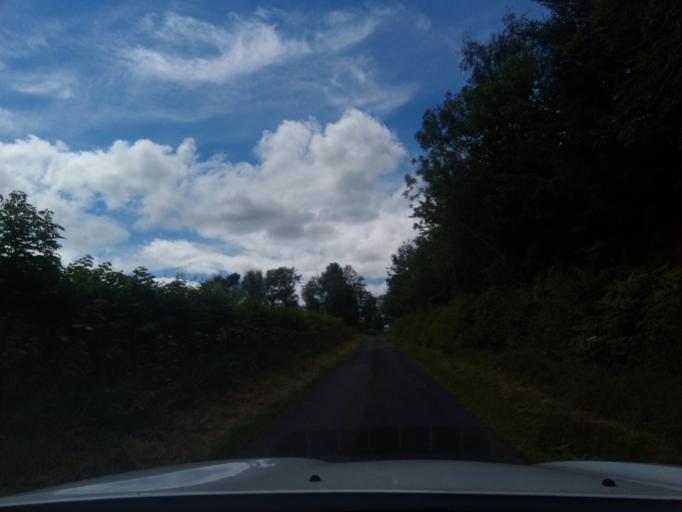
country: GB
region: Scotland
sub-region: The Scottish Borders
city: Jedburgh
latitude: 55.5681
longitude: -2.5535
